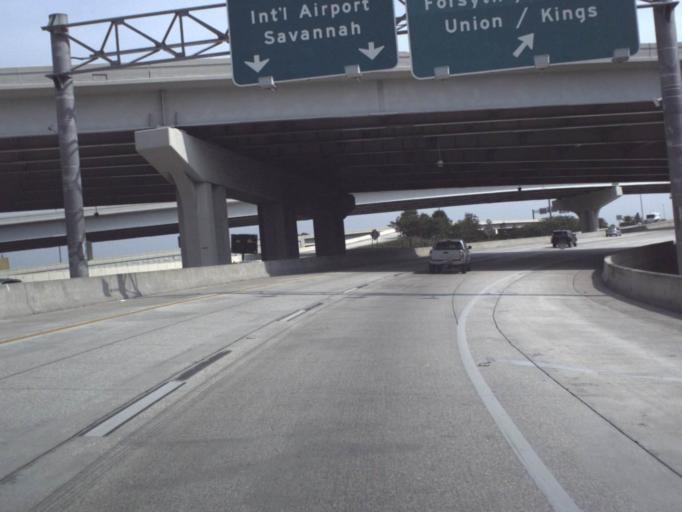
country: US
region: Florida
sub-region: Duval County
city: Jacksonville
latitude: 30.3203
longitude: -81.6815
